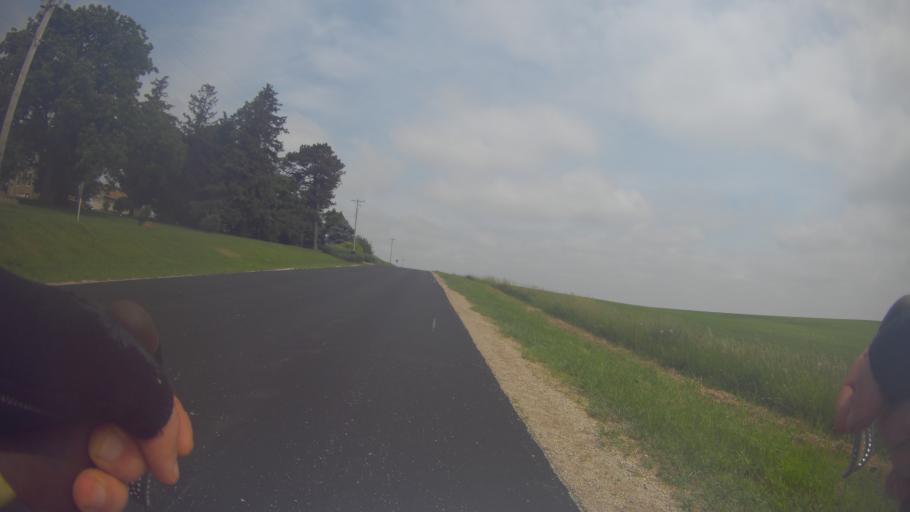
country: US
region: Wisconsin
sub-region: Rock County
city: Edgerton
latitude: 42.9065
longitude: -89.0428
